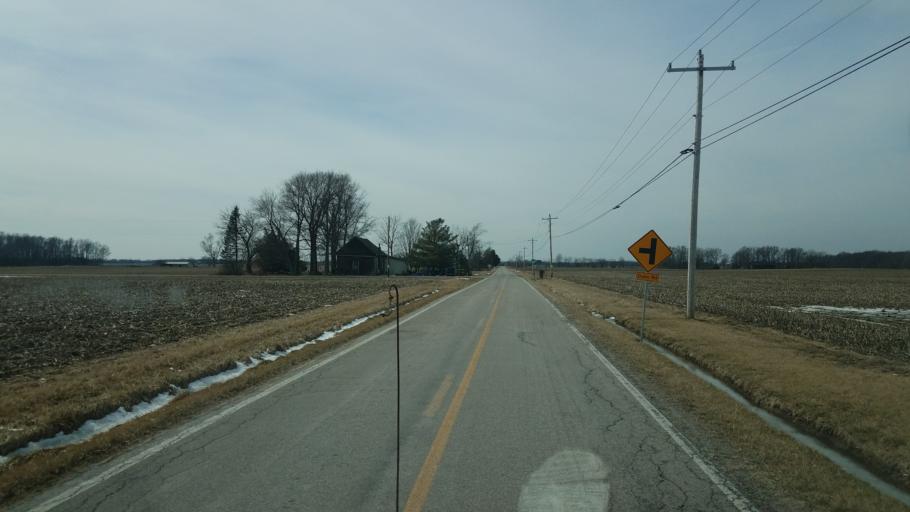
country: US
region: Ohio
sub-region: Delaware County
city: Ashley
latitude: 40.3968
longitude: -82.9931
